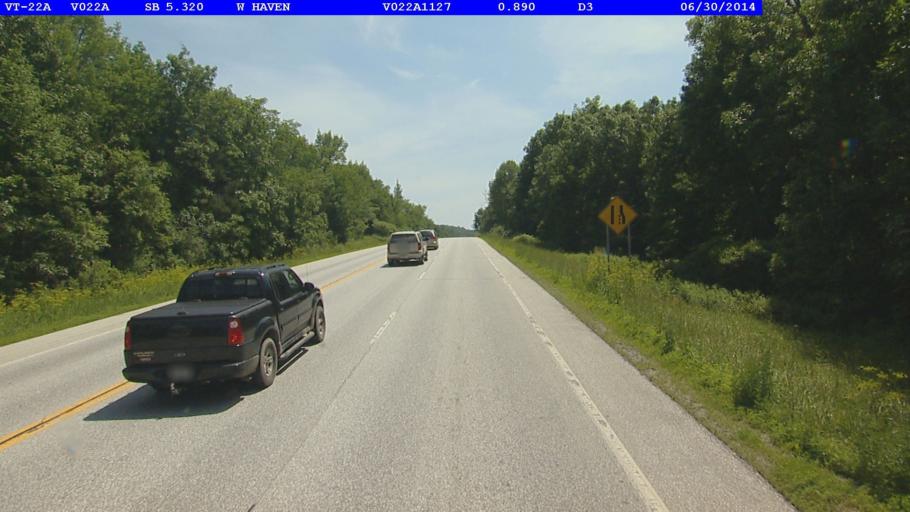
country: US
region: Vermont
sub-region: Rutland County
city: Fair Haven
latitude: 43.6407
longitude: -73.2984
